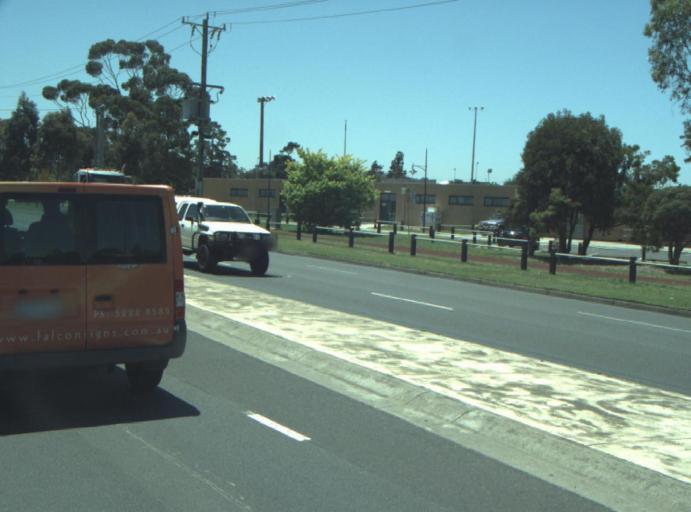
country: AU
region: Victoria
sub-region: Greater Geelong
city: Geelong
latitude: -38.1581
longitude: 144.3506
